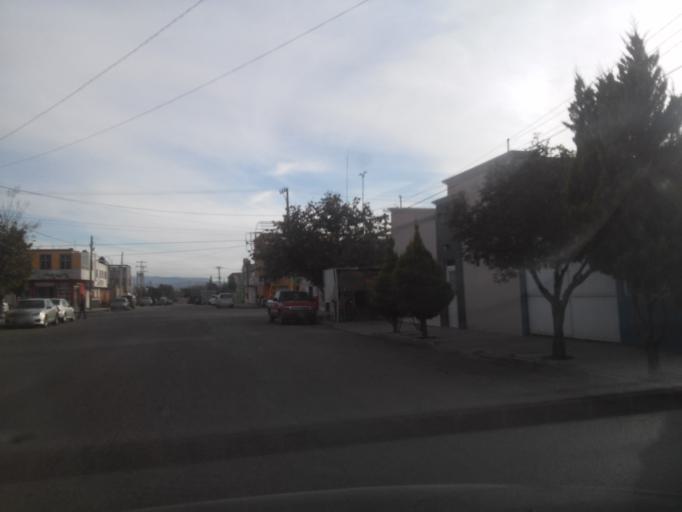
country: MX
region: Durango
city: Victoria de Durango
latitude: 24.0206
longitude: -104.6349
